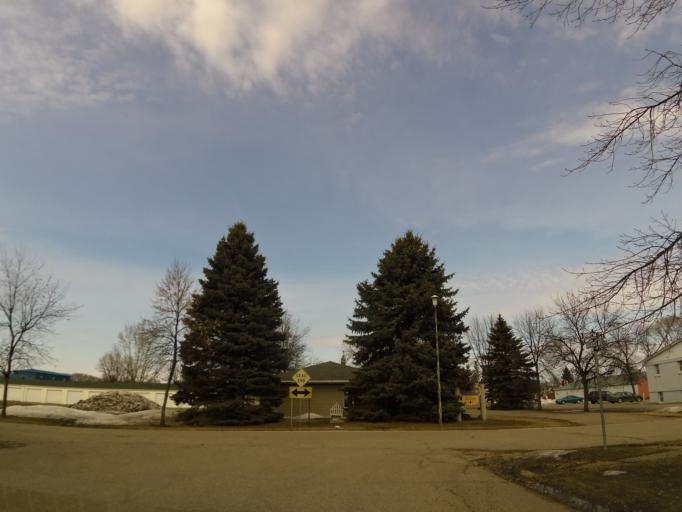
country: US
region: North Dakota
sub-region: Walsh County
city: Grafton
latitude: 48.4108
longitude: -97.4219
